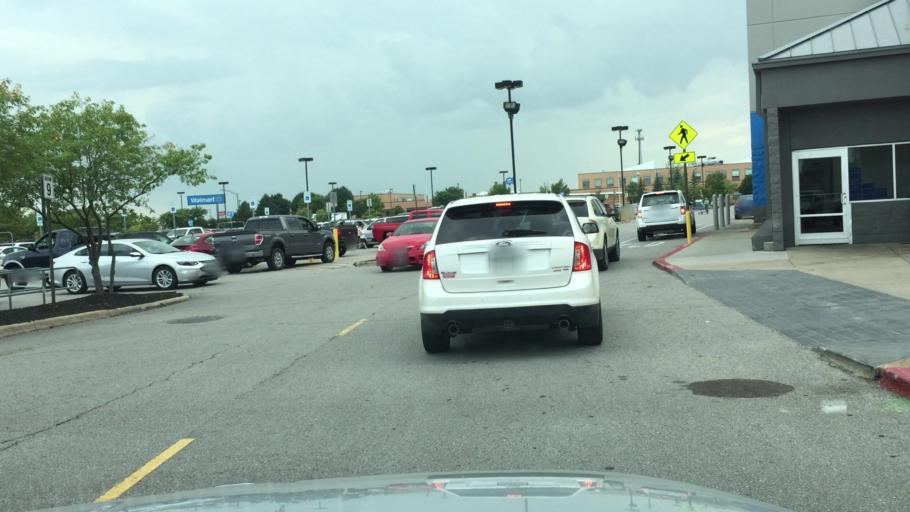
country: US
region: Iowa
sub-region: Johnson County
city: Coralville
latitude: 41.6970
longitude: -91.6115
